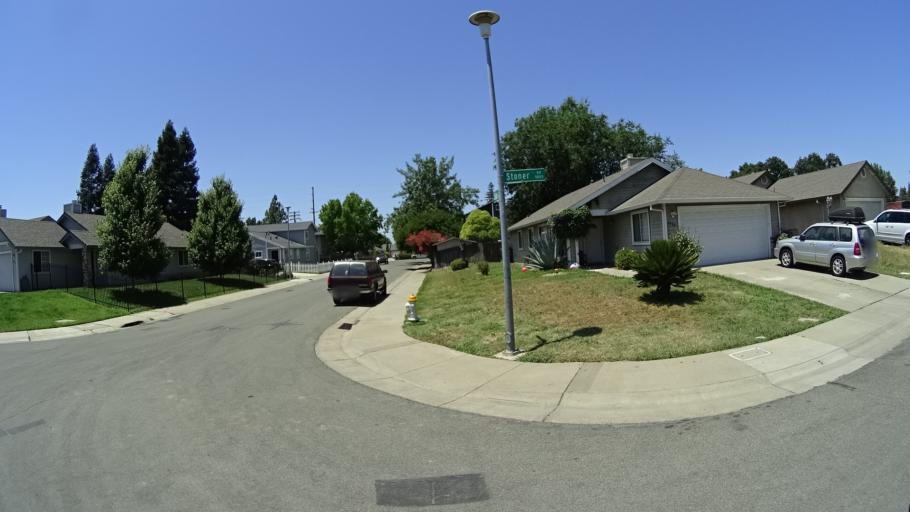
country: US
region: California
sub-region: Sacramento County
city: Florin
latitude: 38.5297
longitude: -121.4284
